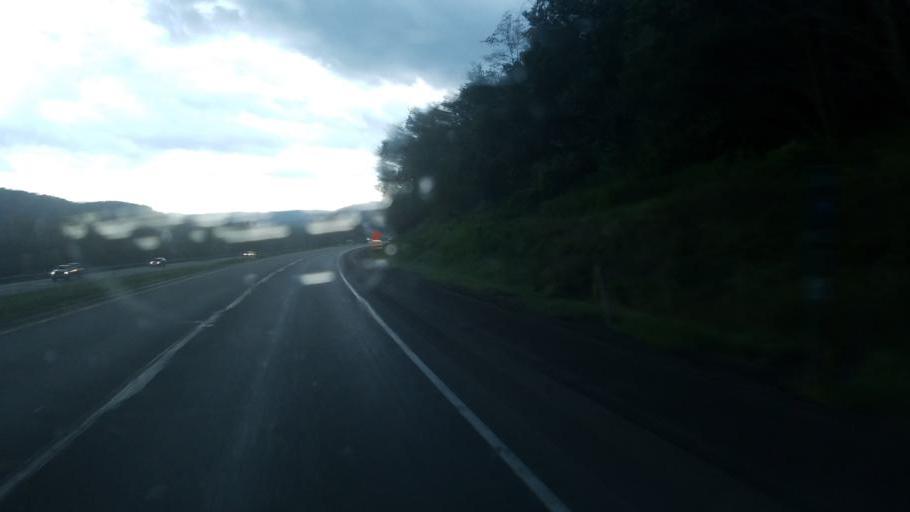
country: US
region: Pennsylvania
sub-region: Butler County
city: Prospect
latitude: 40.8810
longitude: -80.1149
